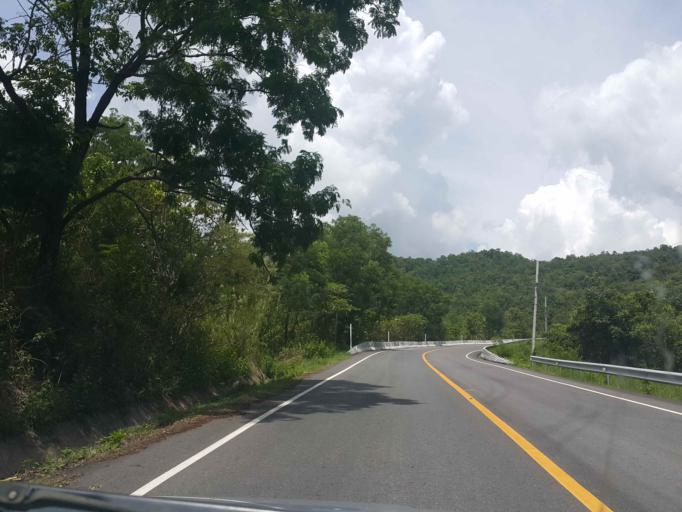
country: TH
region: Phayao
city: Chiang Muan
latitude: 18.8447
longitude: 100.3474
